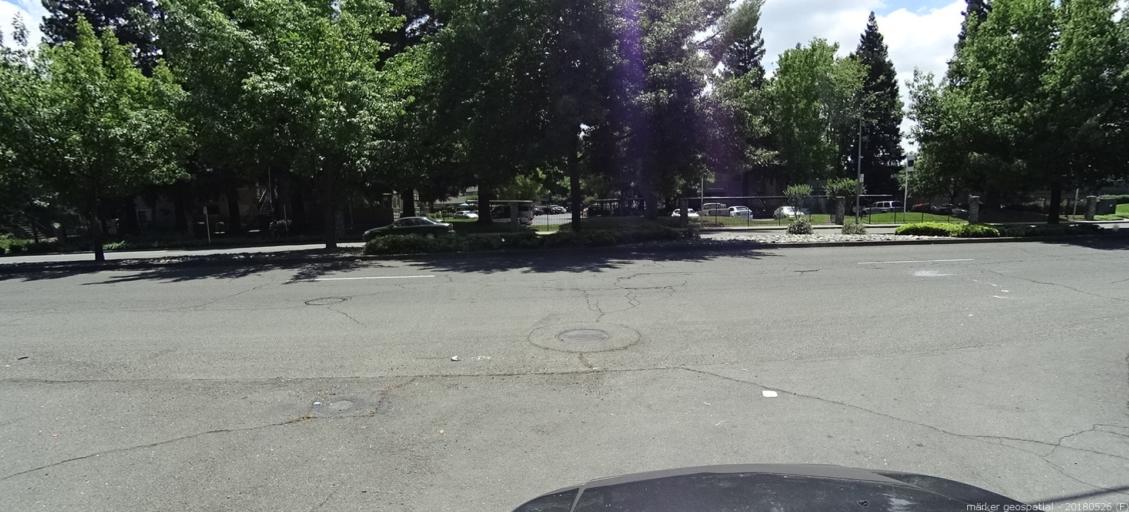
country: US
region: California
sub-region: Sacramento County
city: Sacramento
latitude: 38.6129
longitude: -121.5025
